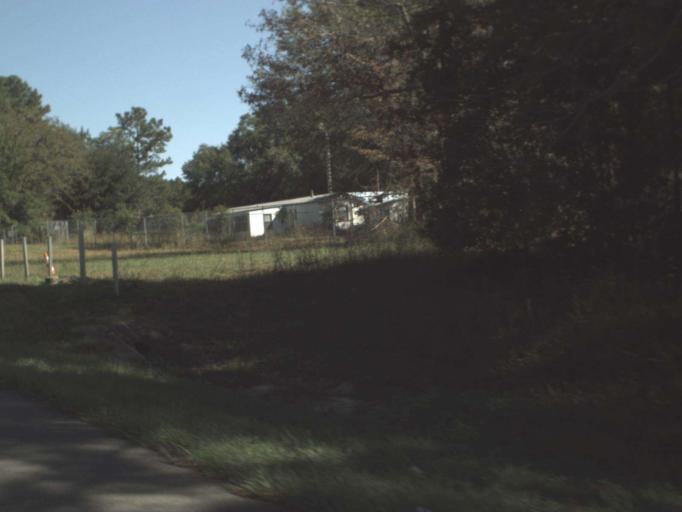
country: US
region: Alabama
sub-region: Covington County
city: Florala
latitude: 30.9670
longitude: -86.3777
